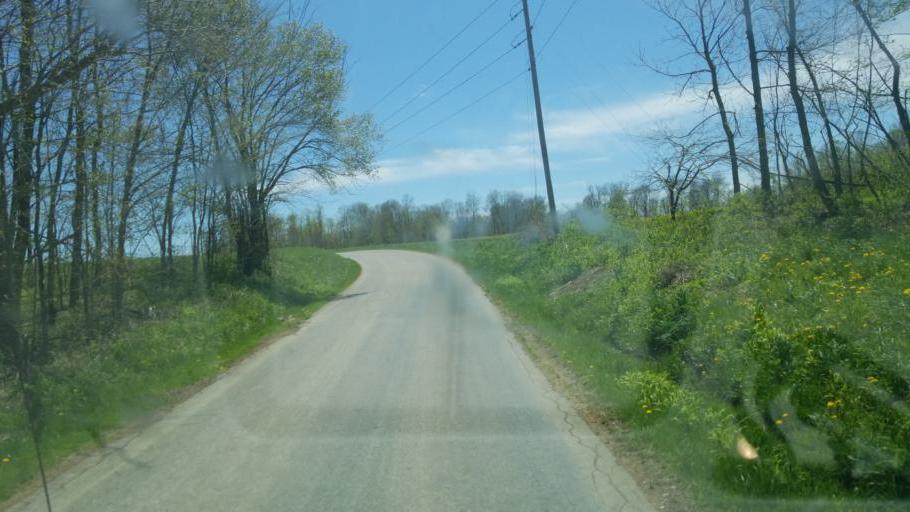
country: US
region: Ohio
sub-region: Knox County
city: Fredericktown
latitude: 40.4918
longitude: -82.6284
